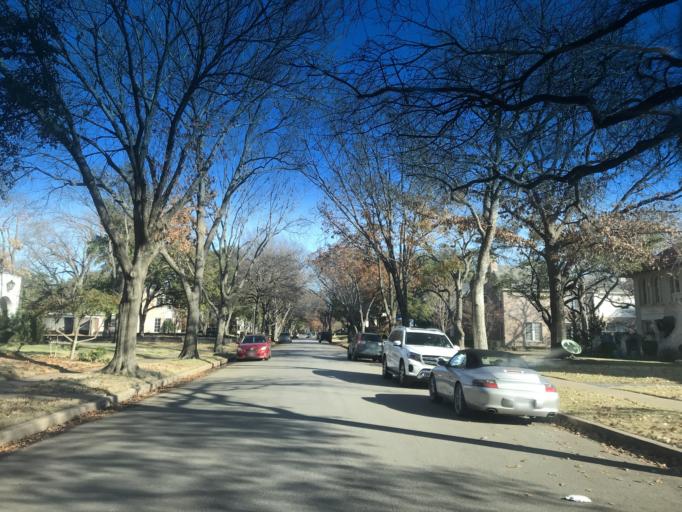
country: US
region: Texas
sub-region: Dallas County
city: Highland Park
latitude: 32.8238
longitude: -96.8100
